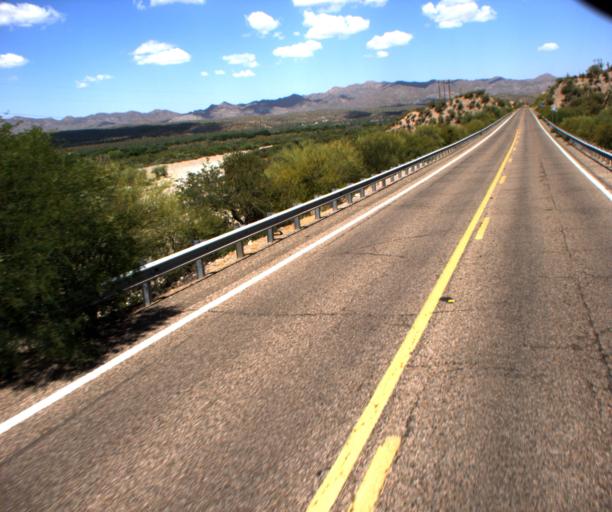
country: US
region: Arizona
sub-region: Pinal County
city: Kearny
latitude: 33.0272
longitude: -110.8673
